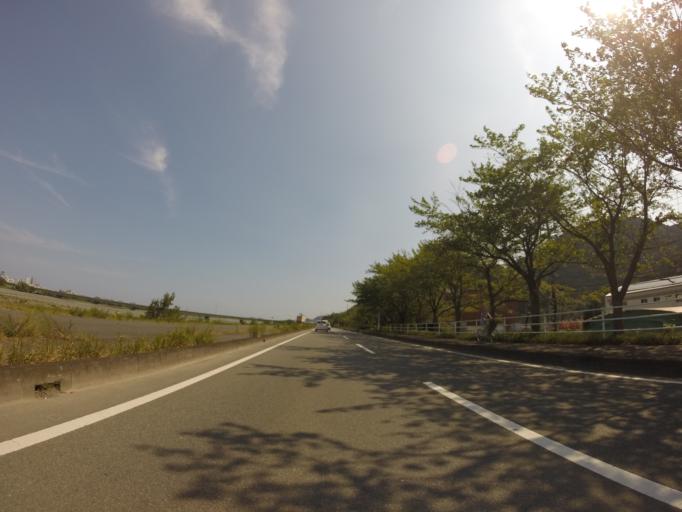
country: JP
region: Shizuoka
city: Shizuoka-shi
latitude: 34.9932
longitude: 138.3547
